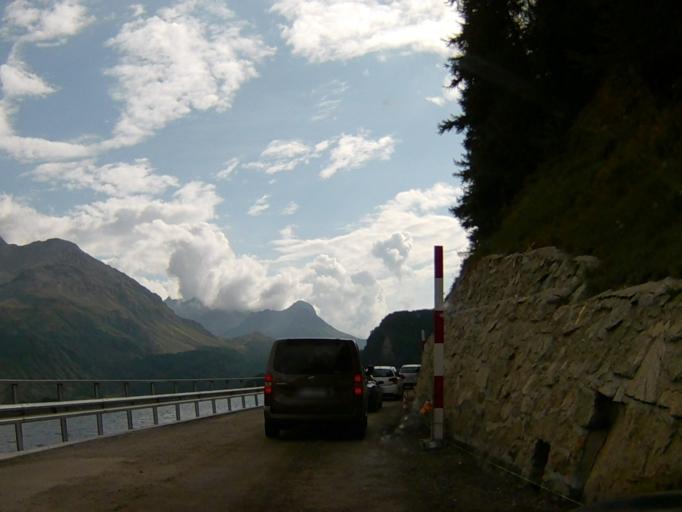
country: CH
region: Grisons
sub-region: Maloja District
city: Silvaplana
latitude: 46.4298
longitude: 9.7386
